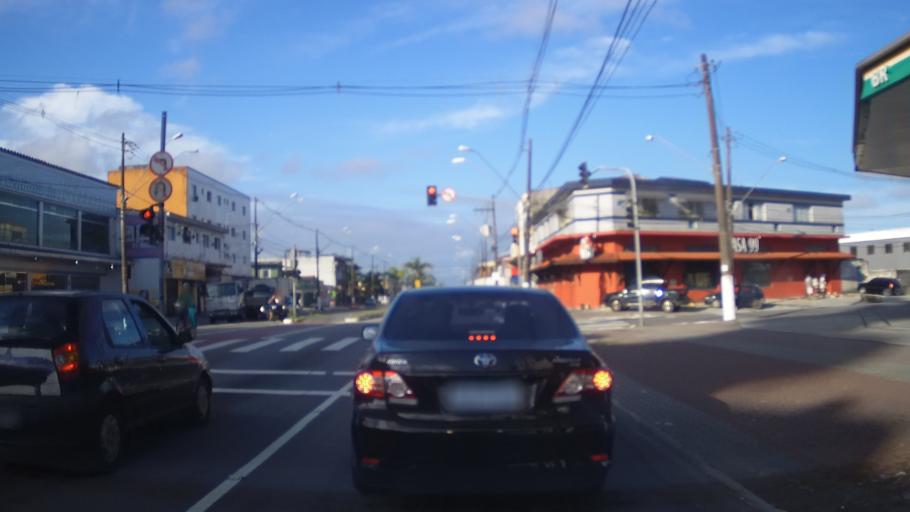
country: BR
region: Sao Paulo
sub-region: Mongagua
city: Mongagua
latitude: -24.0412
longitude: -46.5170
